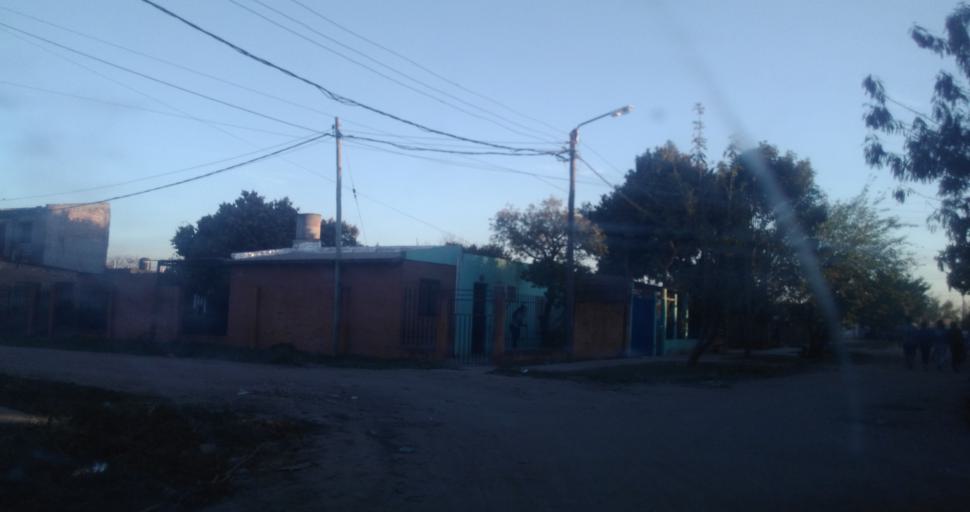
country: AR
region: Chaco
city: Fontana
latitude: -27.4284
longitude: -59.0038
